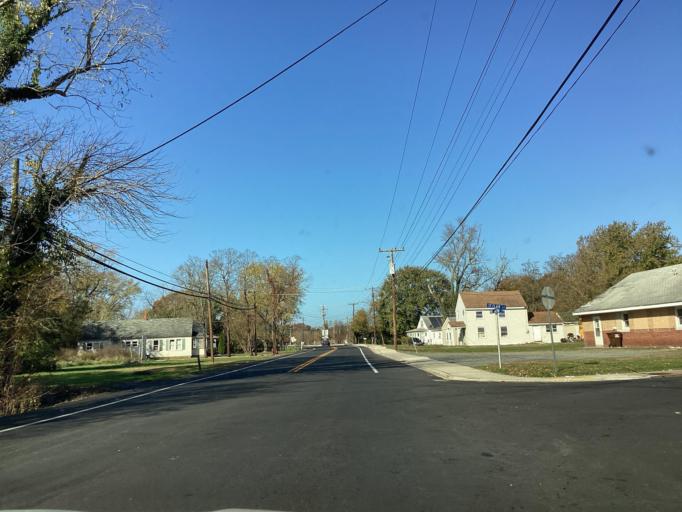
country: US
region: Maryland
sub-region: Dorchester County
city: Cambridge
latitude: 38.5664
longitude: -76.0918
